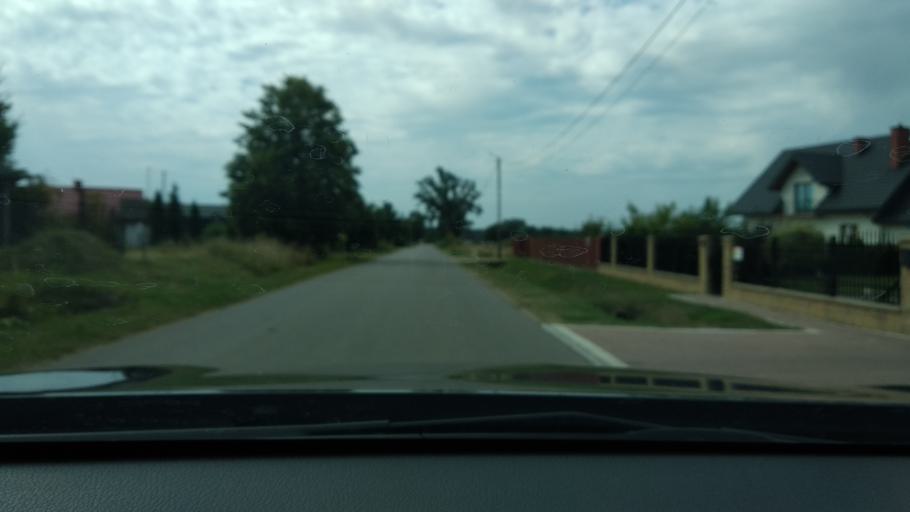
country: PL
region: Masovian Voivodeship
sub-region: Powiat pultuski
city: Zatory
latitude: 52.6530
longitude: 21.1864
